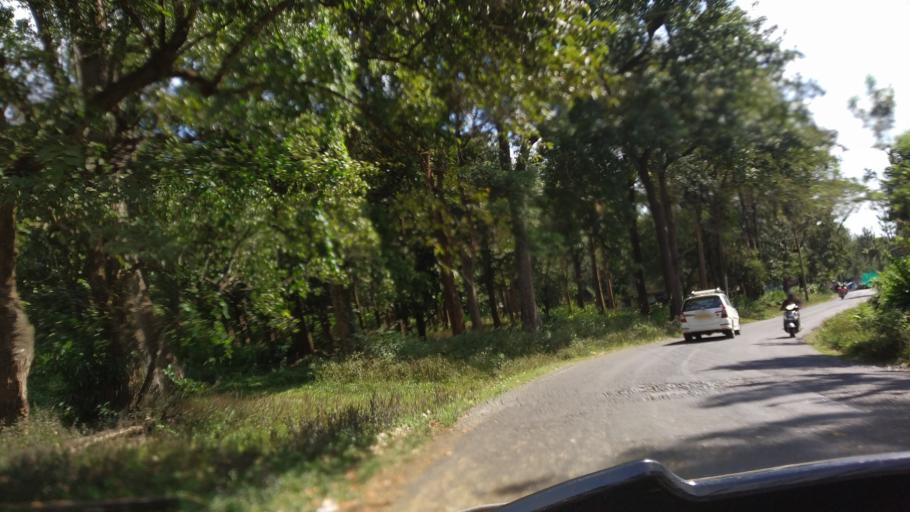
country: IN
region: Kerala
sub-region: Wayanad
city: Panamaram
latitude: 11.9462
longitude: 76.0647
